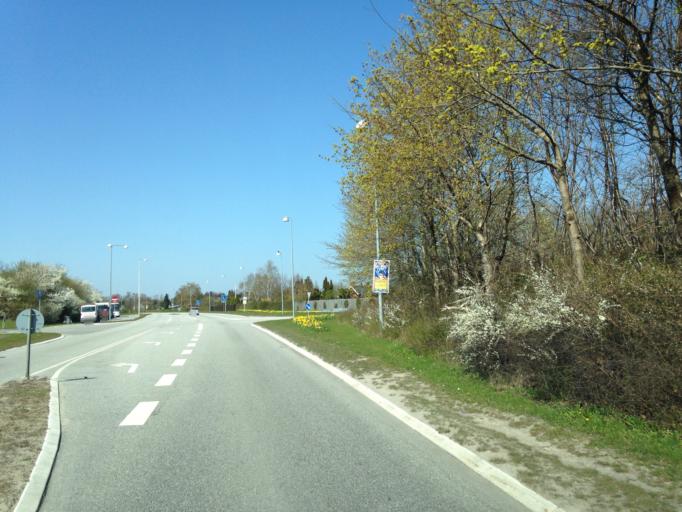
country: DK
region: Zealand
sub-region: Greve Kommune
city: Greve
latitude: 55.5895
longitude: 12.2863
